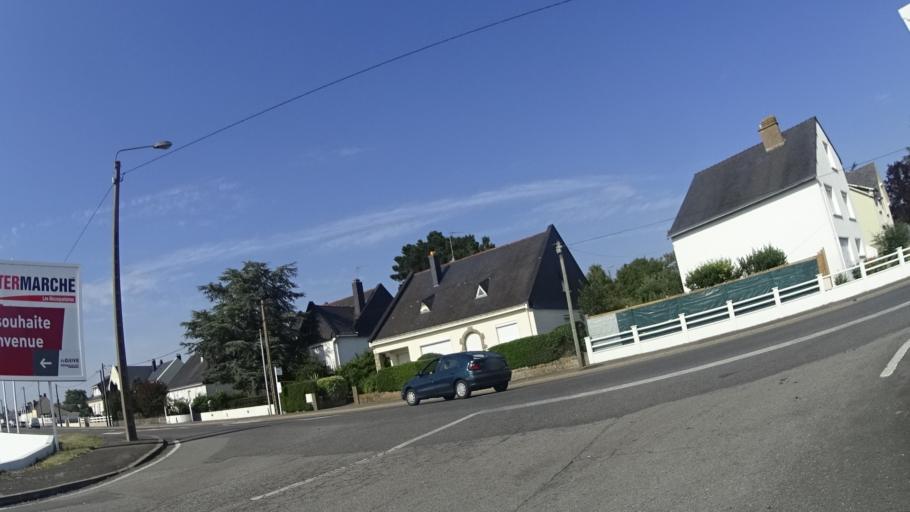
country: FR
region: Pays de la Loire
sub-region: Departement de la Loire-Atlantique
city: Donges
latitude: 47.3231
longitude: -2.0837
